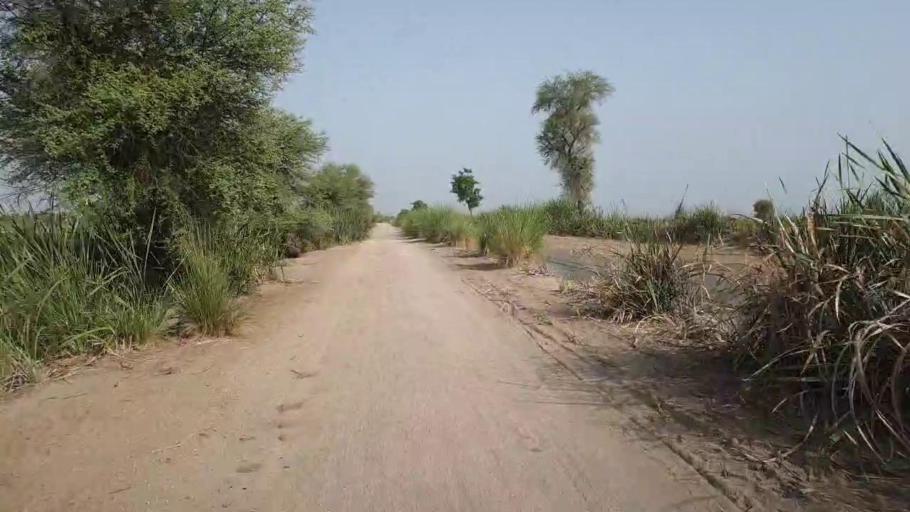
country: PK
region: Sindh
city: Daur
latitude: 26.3348
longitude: 68.1870
